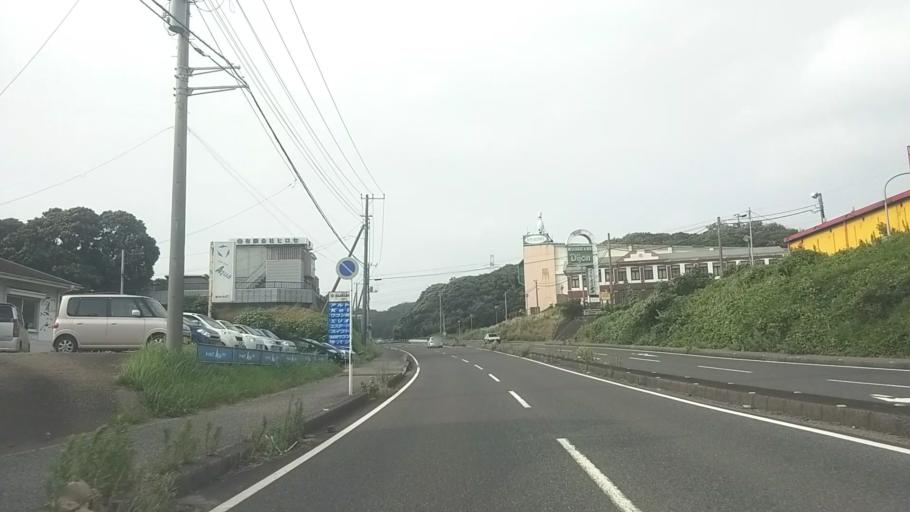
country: JP
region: Chiba
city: Kimitsu
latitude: 35.3385
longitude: 139.8914
